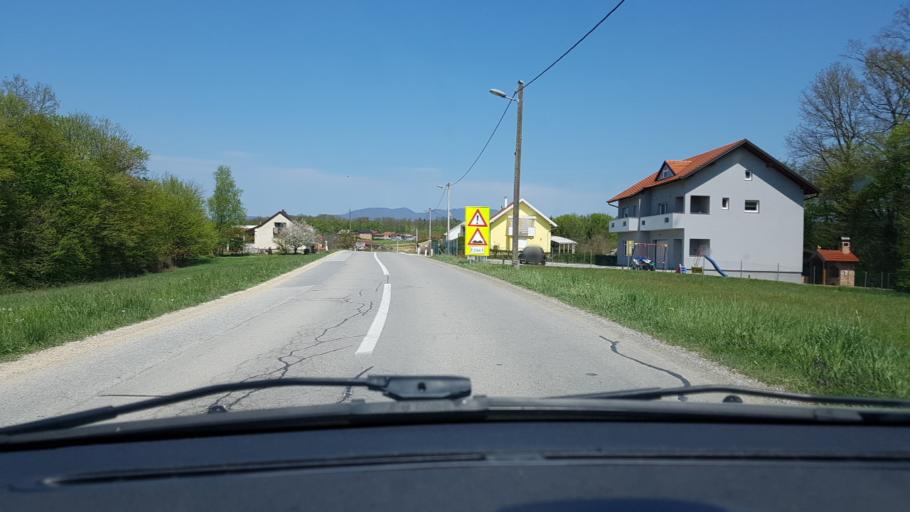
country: HR
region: Krapinsko-Zagorska
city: Zlatar
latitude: 46.0582
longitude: 16.0865
